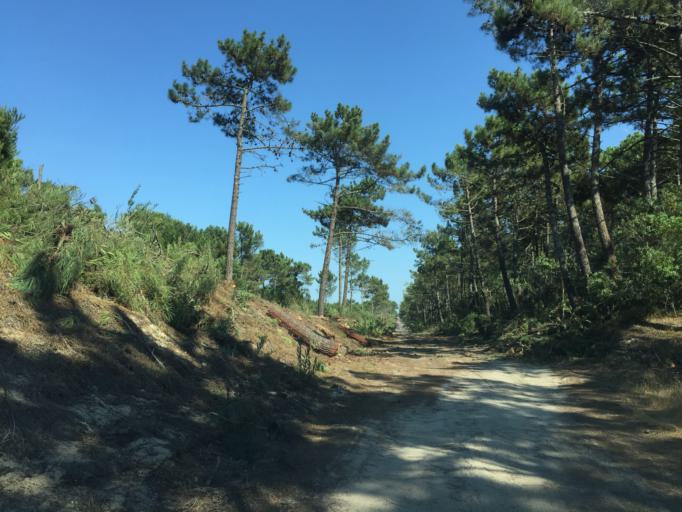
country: PT
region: Coimbra
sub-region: Figueira da Foz
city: Tavarede
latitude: 40.2629
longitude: -8.8612
